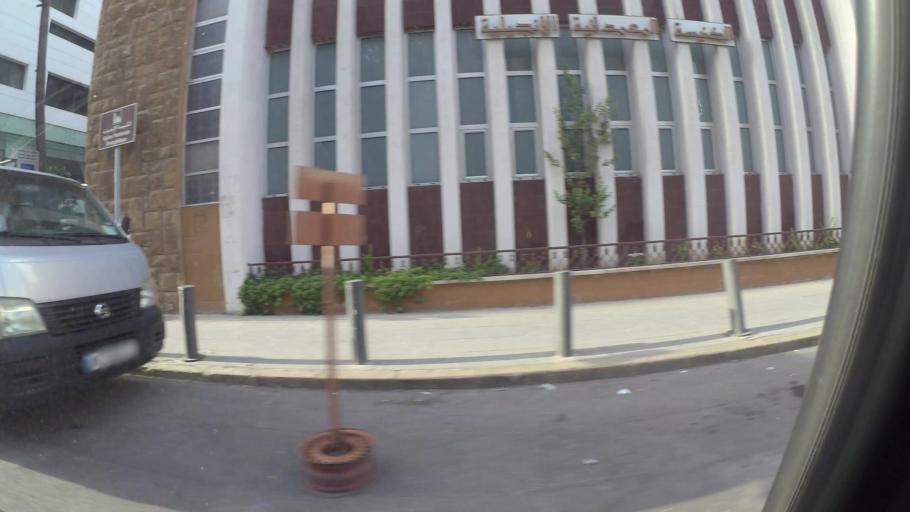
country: LB
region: Beyrouth
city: Ra's Bayrut
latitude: 33.8967
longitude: 35.4862
